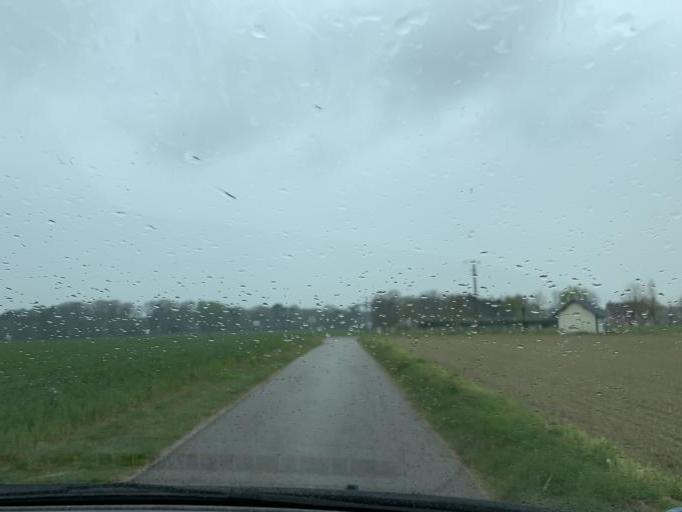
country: FR
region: Haute-Normandie
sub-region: Departement de la Seine-Maritime
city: Etretat
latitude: 49.6889
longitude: 0.2043
